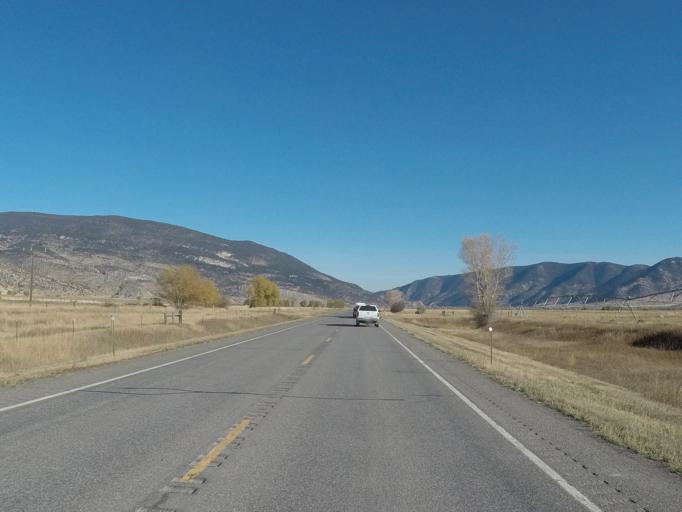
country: US
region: Montana
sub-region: Park County
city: Livingston
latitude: 45.5391
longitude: -110.6019
